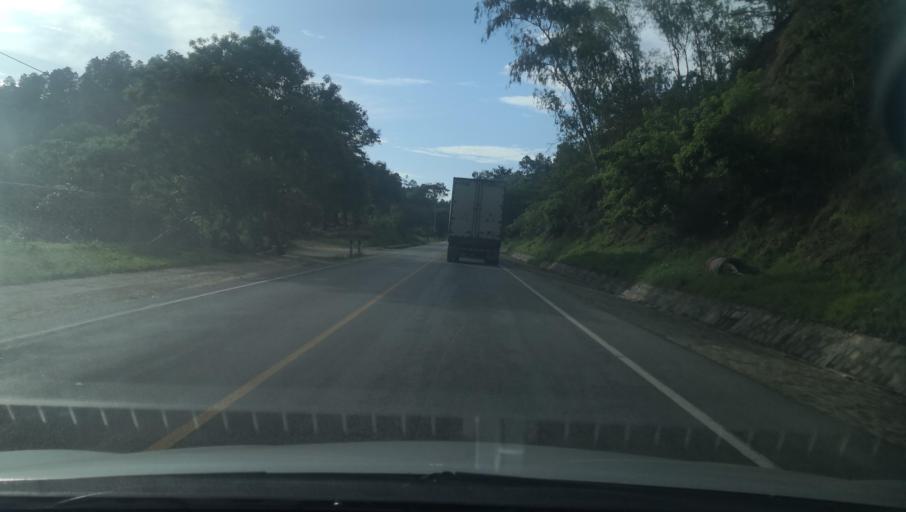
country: NI
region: Nueva Segovia
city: Mozonte
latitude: 13.7219
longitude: -86.5059
